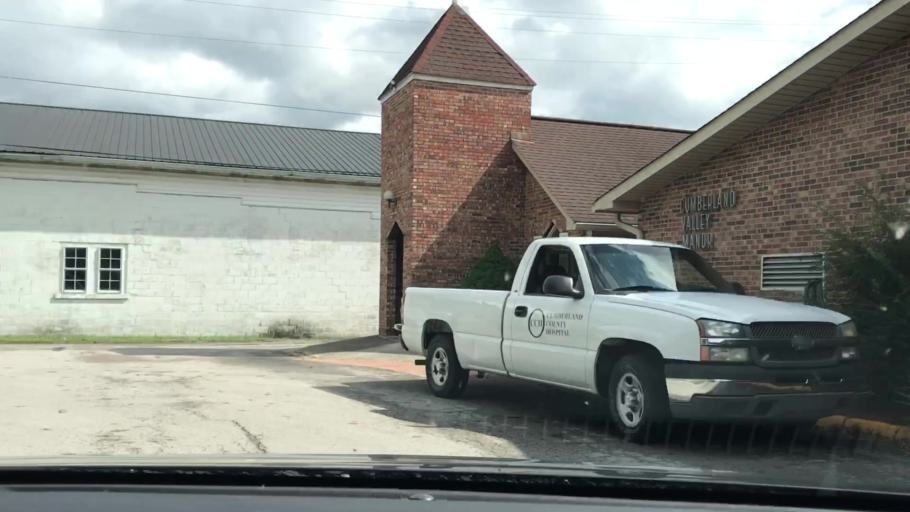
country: US
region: Kentucky
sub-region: Cumberland County
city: Burkesville
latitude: 36.7879
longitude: -85.3720
